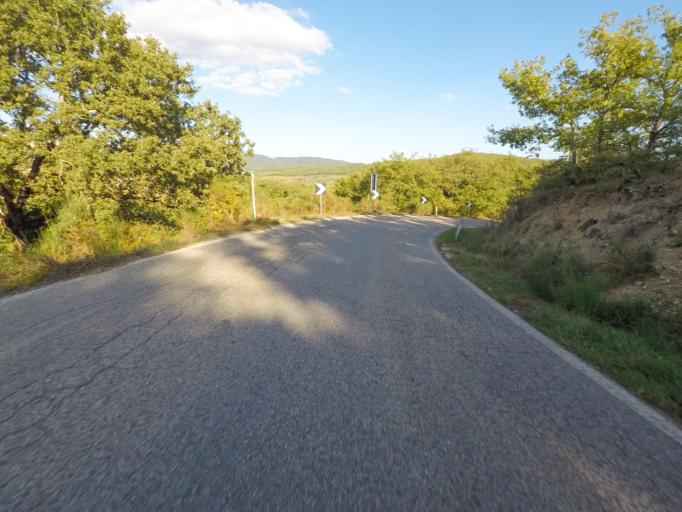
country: IT
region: Tuscany
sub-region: Provincia di Siena
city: Radda in Chianti
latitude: 43.4782
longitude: 11.3712
